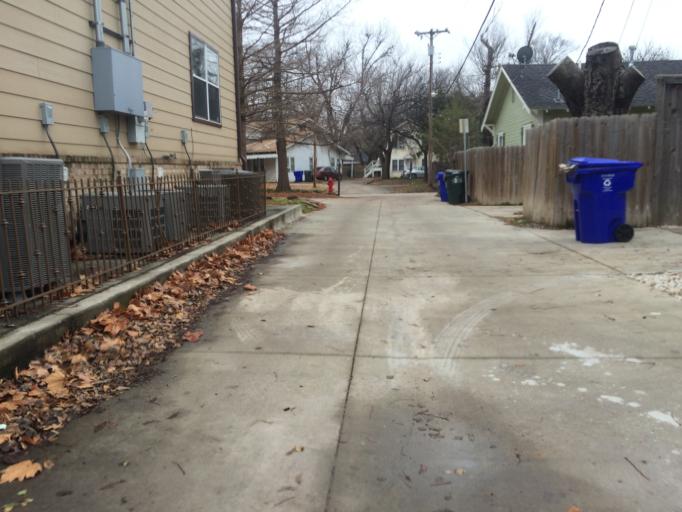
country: US
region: Oklahoma
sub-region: Cleveland County
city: Norman
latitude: 35.2149
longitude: -97.4476
